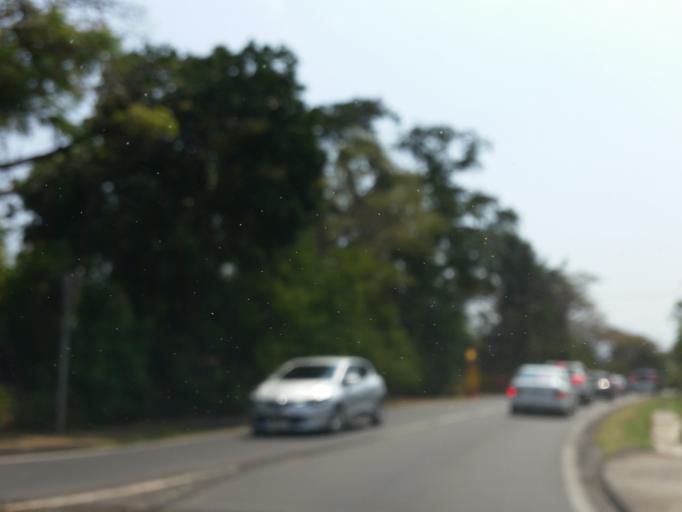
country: RE
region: Reunion
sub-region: Reunion
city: Sainte-Marie
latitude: -20.9021
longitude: 55.5077
